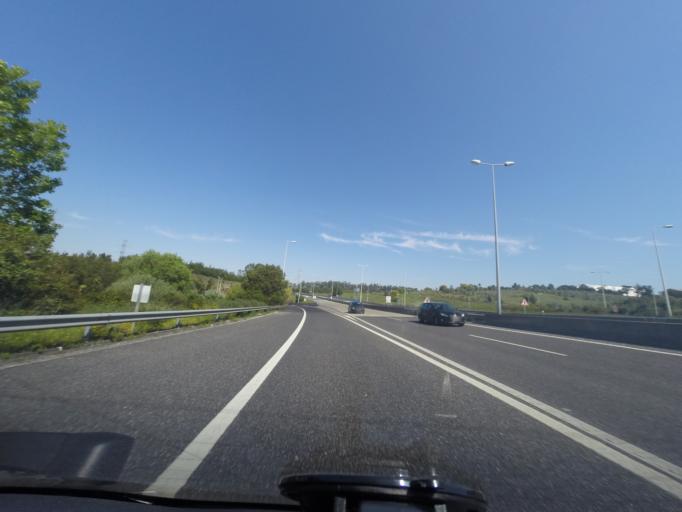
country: PT
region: Lisbon
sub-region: Odivelas
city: Canecas
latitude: 38.7906
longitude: -9.2379
